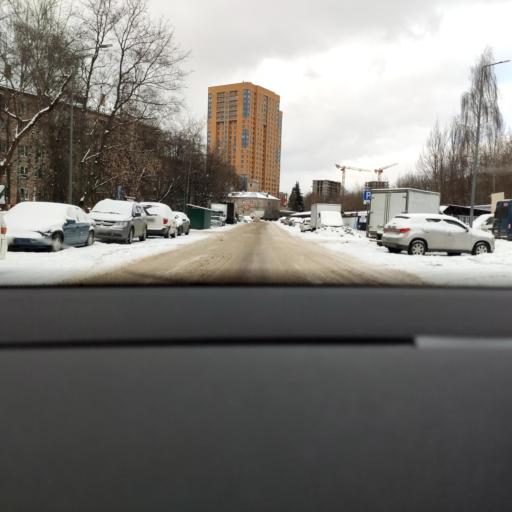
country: RU
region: Moskovskaya
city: Reutov
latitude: 55.7626
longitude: 37.8675
